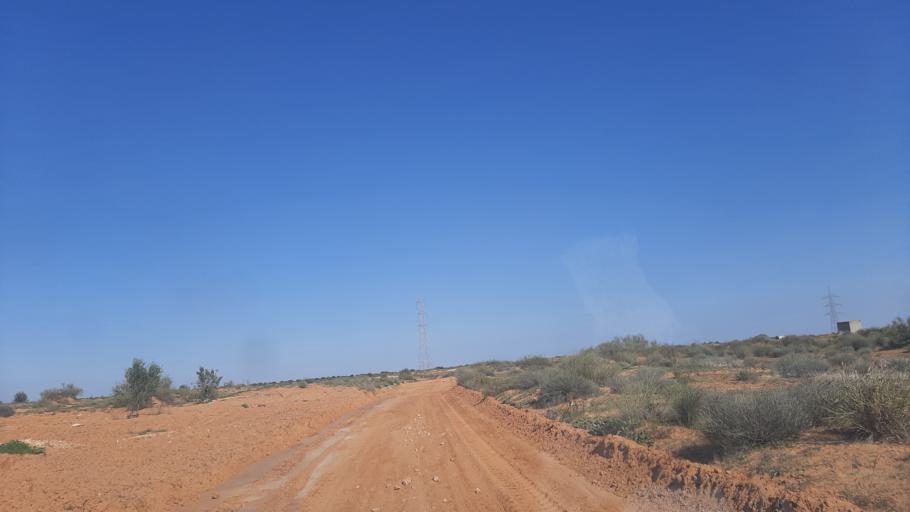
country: TN
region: Madanin
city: Medenine
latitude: 33.2767
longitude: 10.7727
